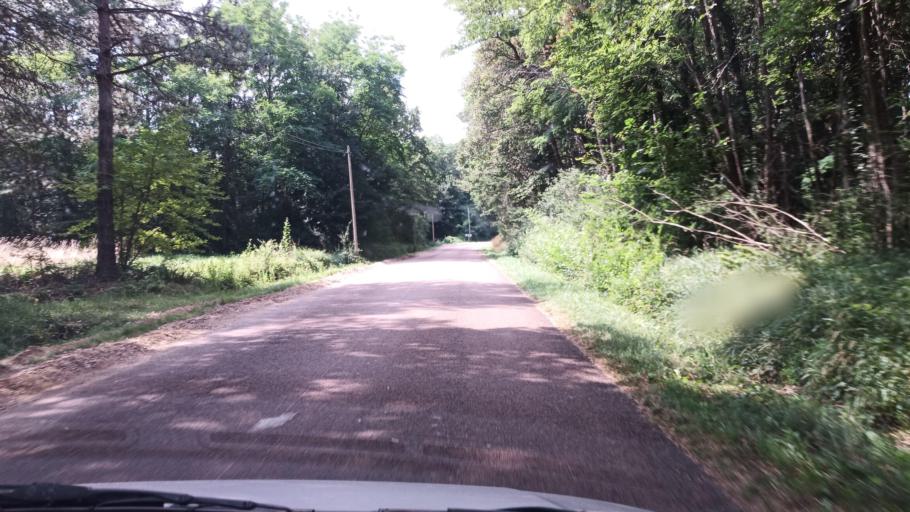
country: FR
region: Bourgogne
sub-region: Departement de l'Yonne
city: Saint-Julien-du-Sault
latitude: 48.0517
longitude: 3.2248
